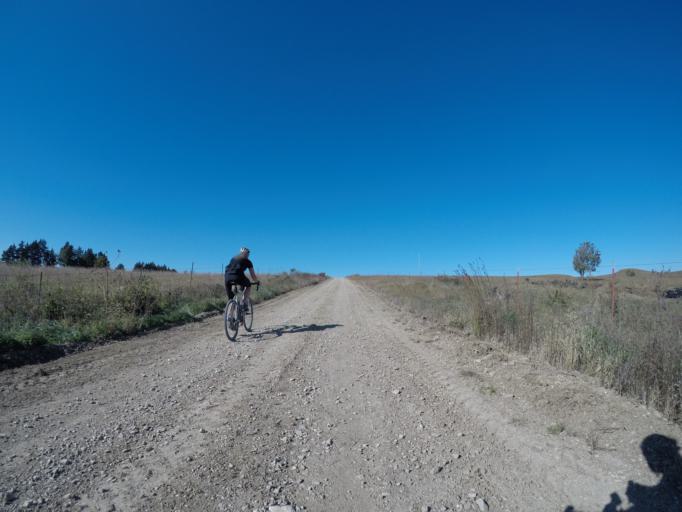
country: US
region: Kansas
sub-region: Wabaunsee County
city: Alma
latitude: 38.9132
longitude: -96.3660
